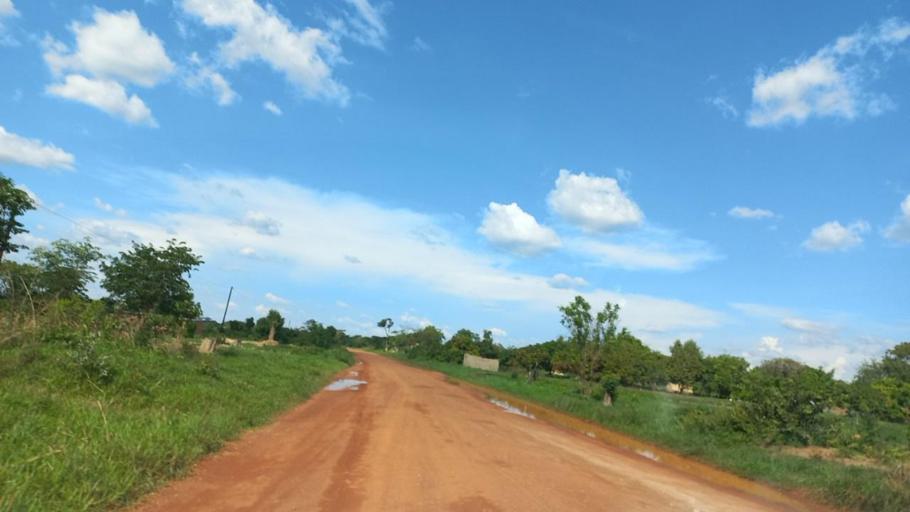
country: ZM
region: Copperbelt
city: Kitwe
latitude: -12.8562
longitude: 28.3865
